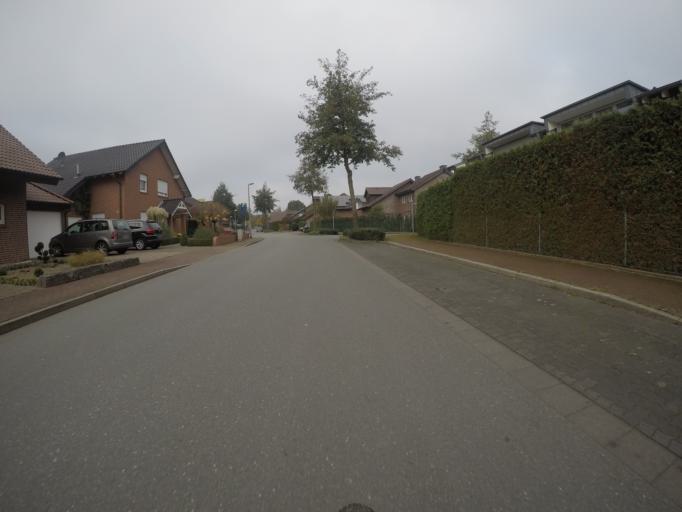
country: DE
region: North Rhine-Westphalia
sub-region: Regierungsbezirk Dusseldorf
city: Bocholt
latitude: 51.8352
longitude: 6.5954
